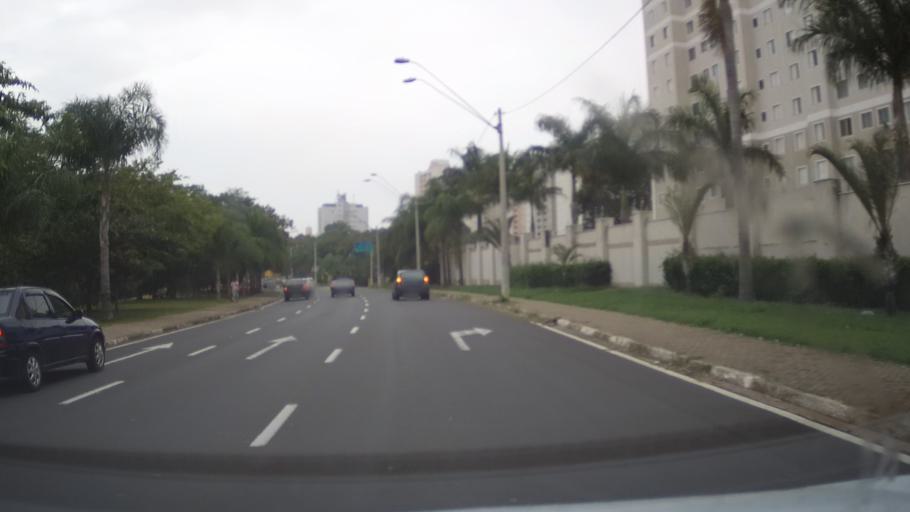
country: BR
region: Sao Paulo
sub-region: Campinas
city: Campinas
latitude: -22.9293
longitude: -47.0592
